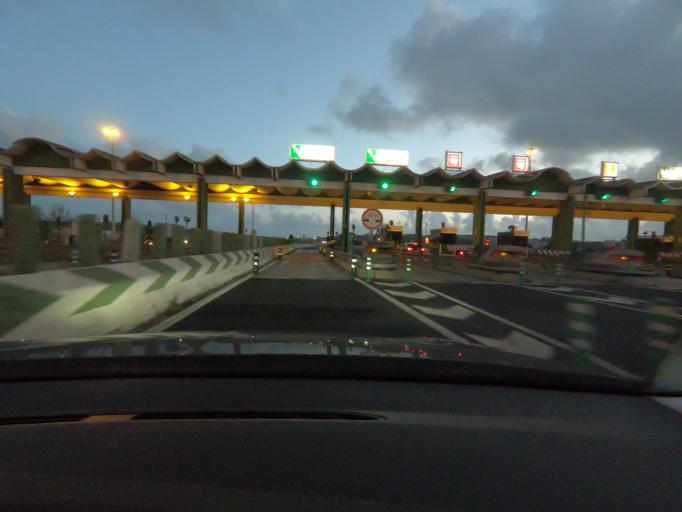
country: PT
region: Lisbon
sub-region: Oeiras
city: Barcarena
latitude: 38.7459
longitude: -9.2744
